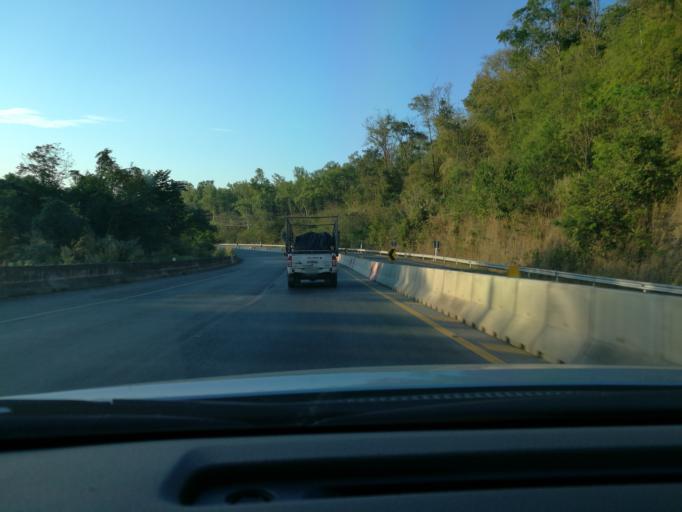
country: TH
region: Phitsanulok
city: Wang Thong
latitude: 16.8544
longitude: 100.5106
